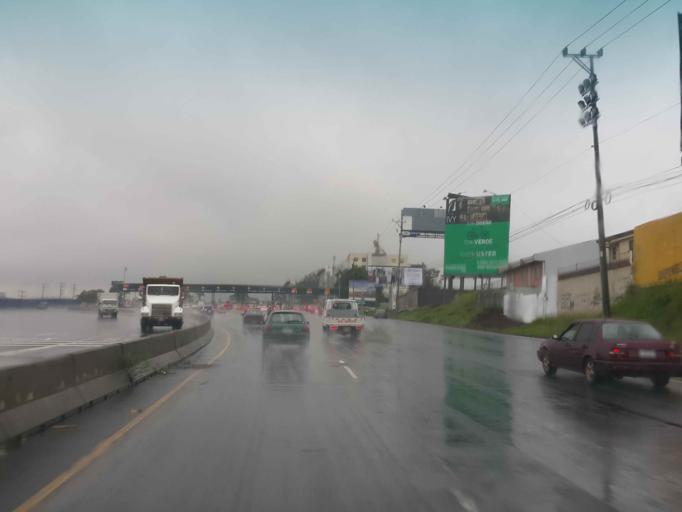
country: CR
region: San Jose
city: San Rafael
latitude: 9.9375
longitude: -84.1360
